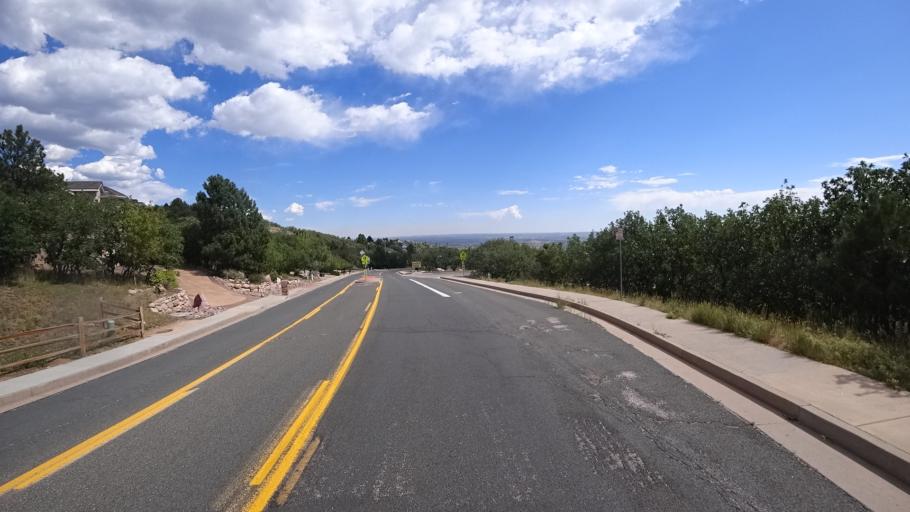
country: US
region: Colorado
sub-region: El Paso County
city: Fort Carson
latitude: 38.7592
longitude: -104.8255
